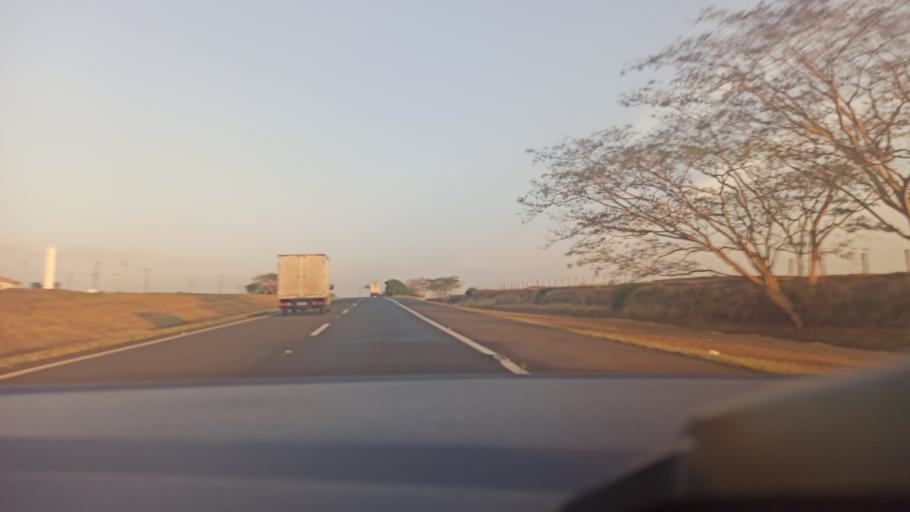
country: BR
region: Sao Paulo
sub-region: Santa Adelia
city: Santa Adelia
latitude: -21.3759
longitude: -48.7426
